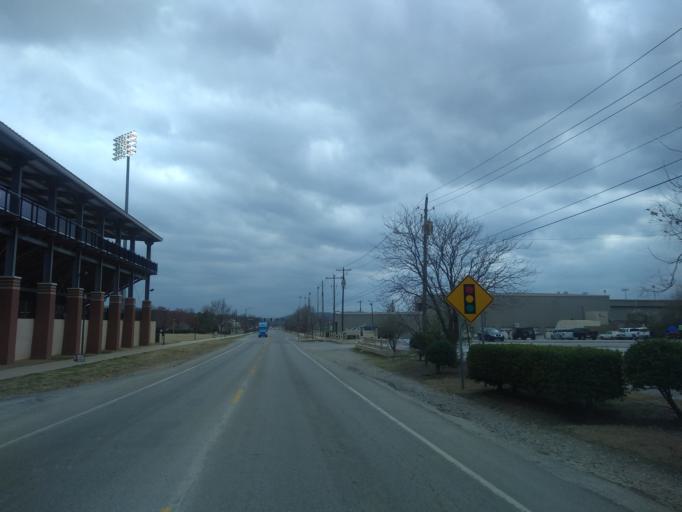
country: US
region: Arkansas
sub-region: Washington County
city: Fayetteville
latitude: 36.0629
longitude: -94.1803
